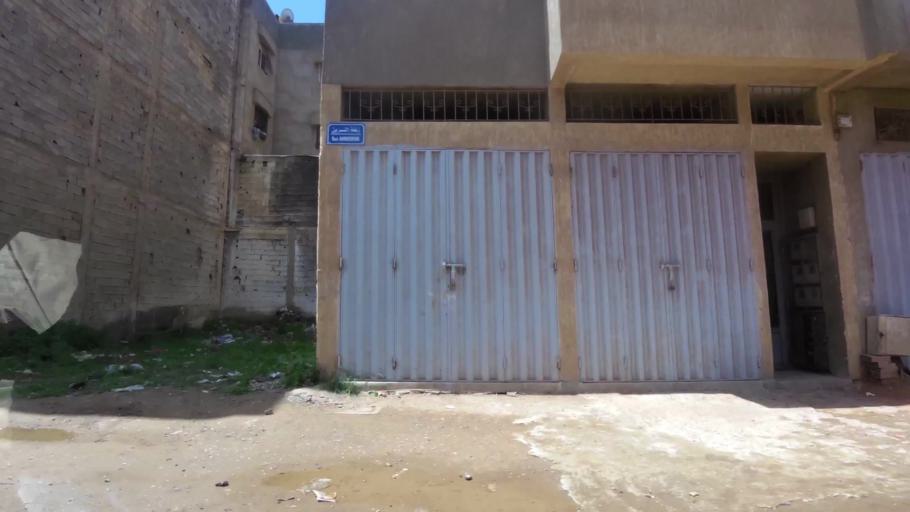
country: MA
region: Grand Casablanca
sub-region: Nouaceur
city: Dar Bouazza
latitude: 33.5306
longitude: -7.7326
